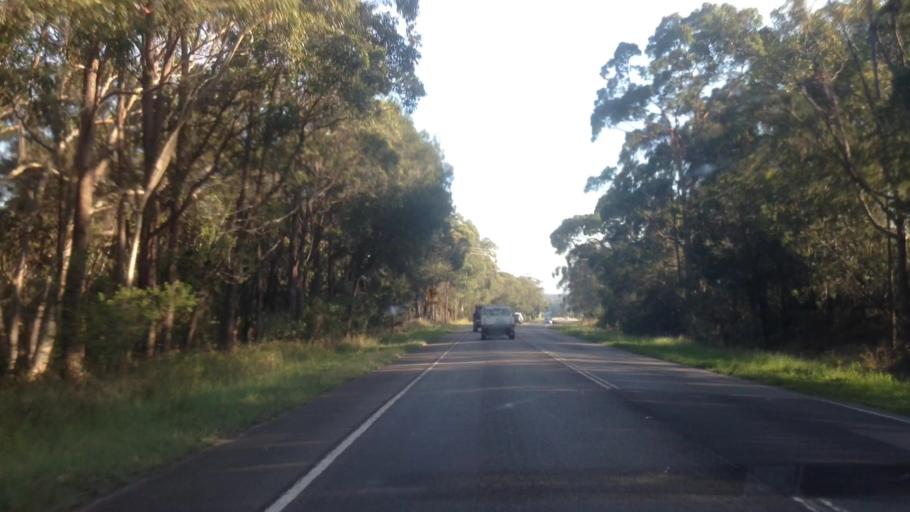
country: AU
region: New South Wales
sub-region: Lake Macquarie Shire
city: Dora Creek
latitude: -33.1513
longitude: 151.4793
